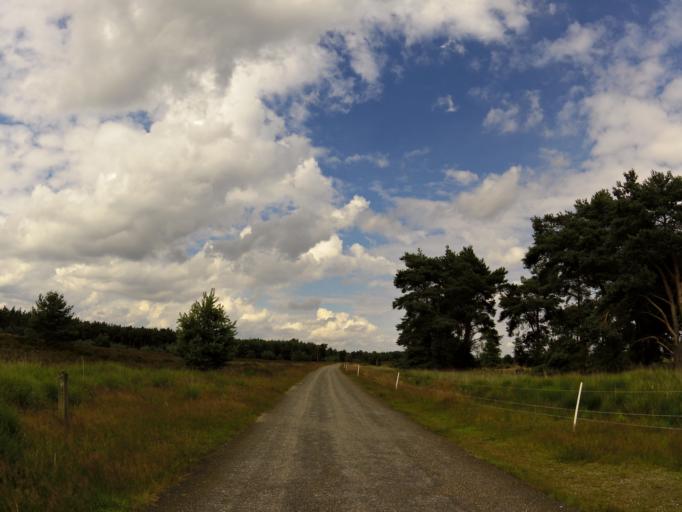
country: NL
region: North Brabant
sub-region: Gemeente Valkenswaard
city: Valkenswaard
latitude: 51.3072
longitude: 5.5071
